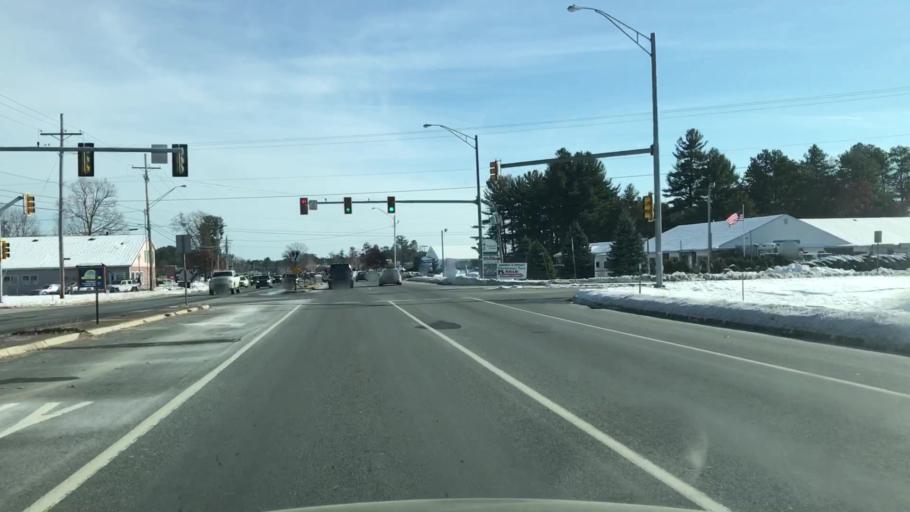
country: US
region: New Hampshire
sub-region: Hillsborough County
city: Hollis
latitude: 42.8095
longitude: -71.5737
